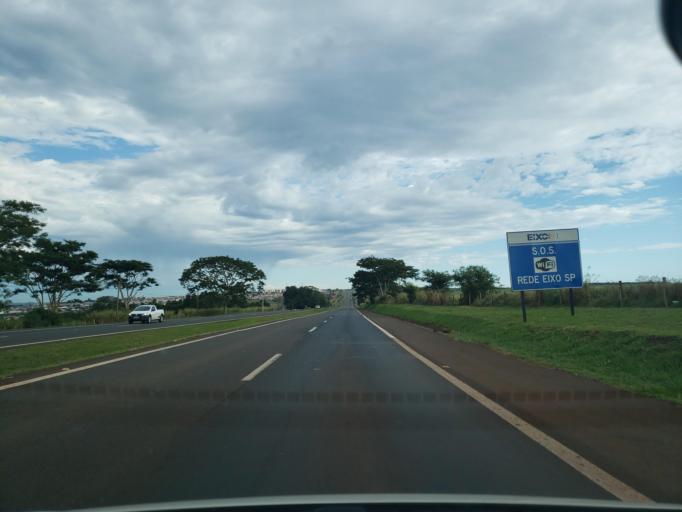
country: BR
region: Sao Paulo
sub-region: Jau
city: Jau
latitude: -22.2639
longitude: -48.5261
